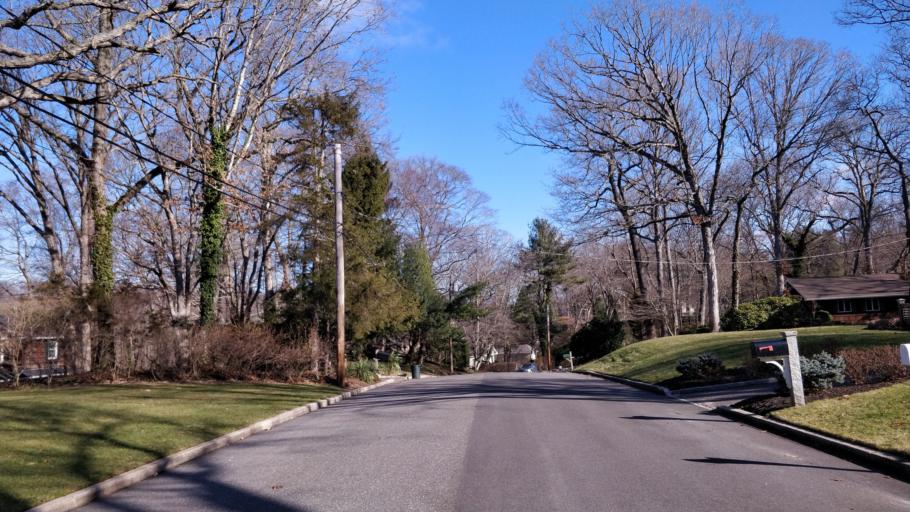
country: US
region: New York
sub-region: Suffolk County
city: Smithtown
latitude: 40.8608
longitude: -73.2049
